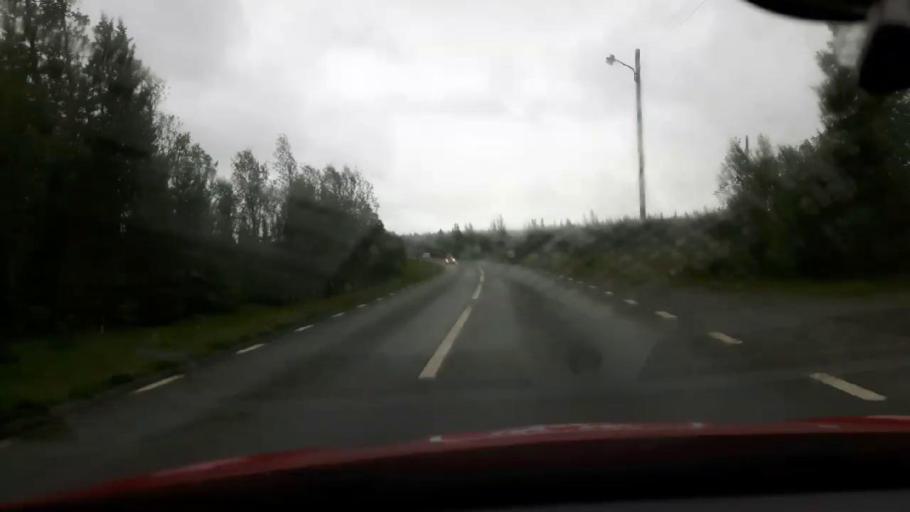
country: SE
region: Jaemtland
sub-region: Are Kommun
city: Are
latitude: 63.3174
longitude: 12.5053
